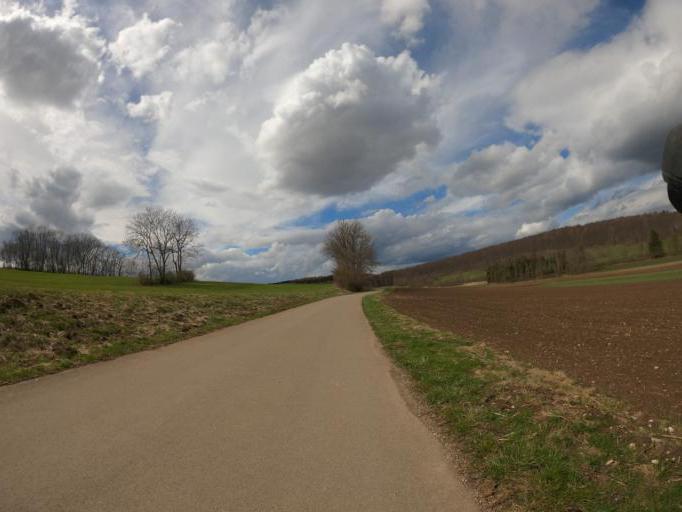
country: DE
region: Baden-Wuerttemberg
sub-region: Tuebingen Region
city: Pfullingen
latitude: 48.3995
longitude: 9.1691
